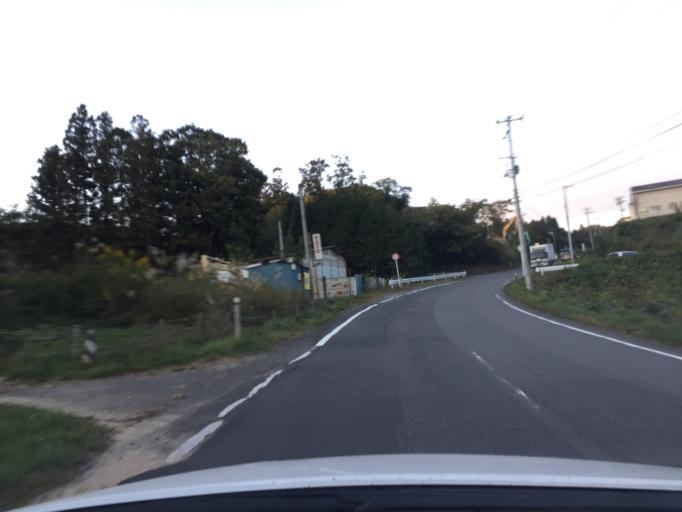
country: JP
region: Fukushima
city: Sukagawa
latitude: 37.3313
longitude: 140.4399
